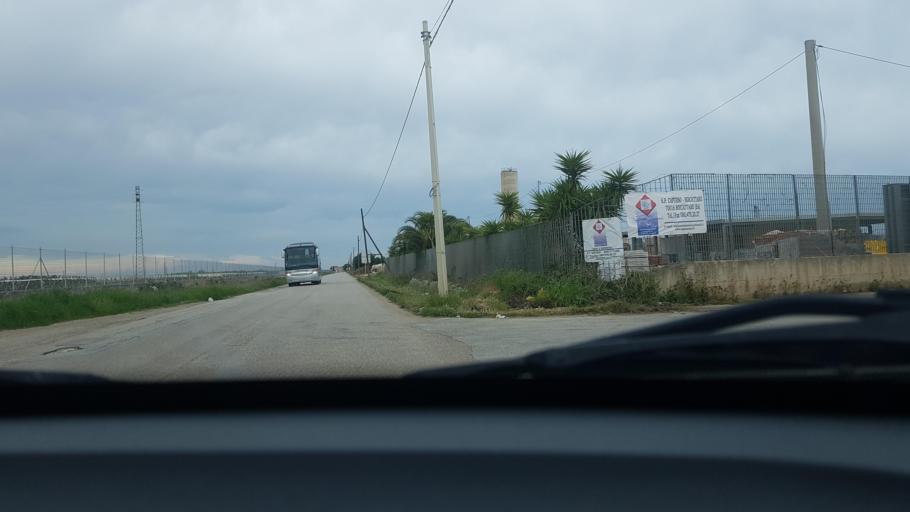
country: IT
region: Apulia
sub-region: Provincia di Bari
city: Noicattaro
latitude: 41.0349
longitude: 16.9744
